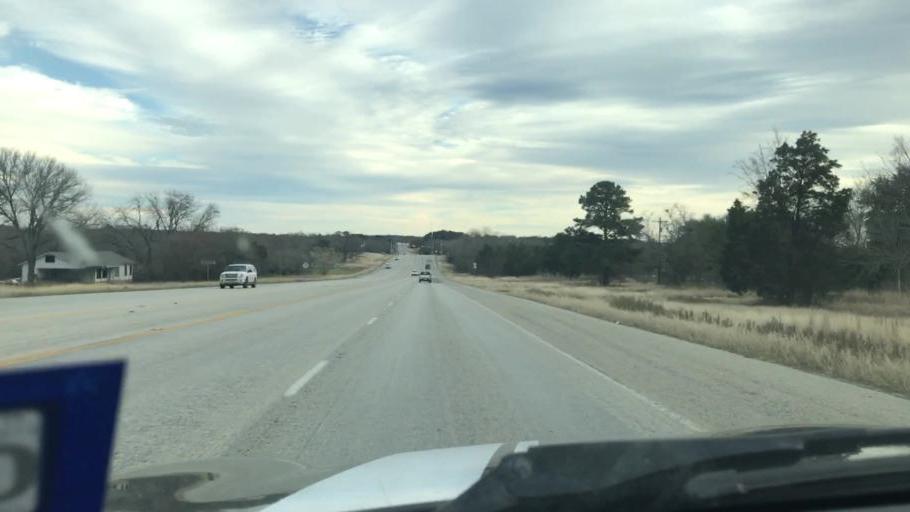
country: US
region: Texas
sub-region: Bastrop County
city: Camp Swift
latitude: 30.2838
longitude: -97.2454
